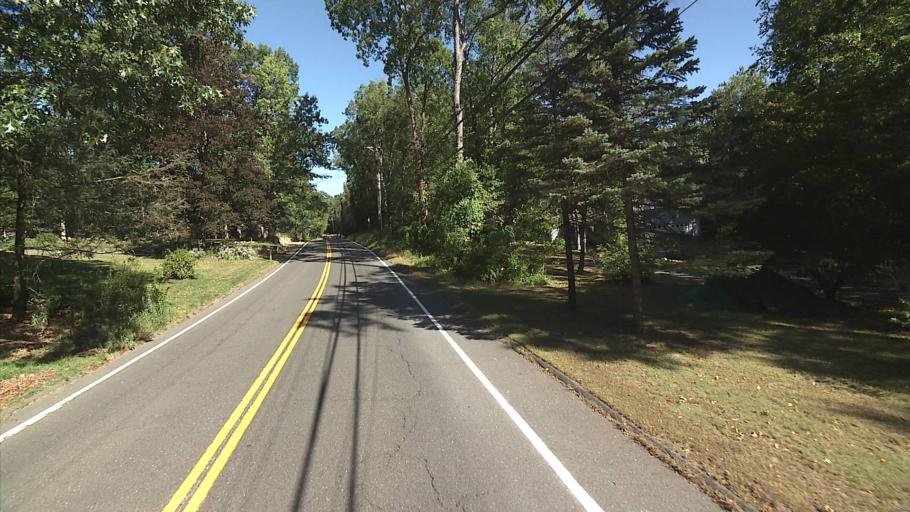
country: US
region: Connecticut
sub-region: Hartford County
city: Bristol
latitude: 41.7216
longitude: -72.9483
